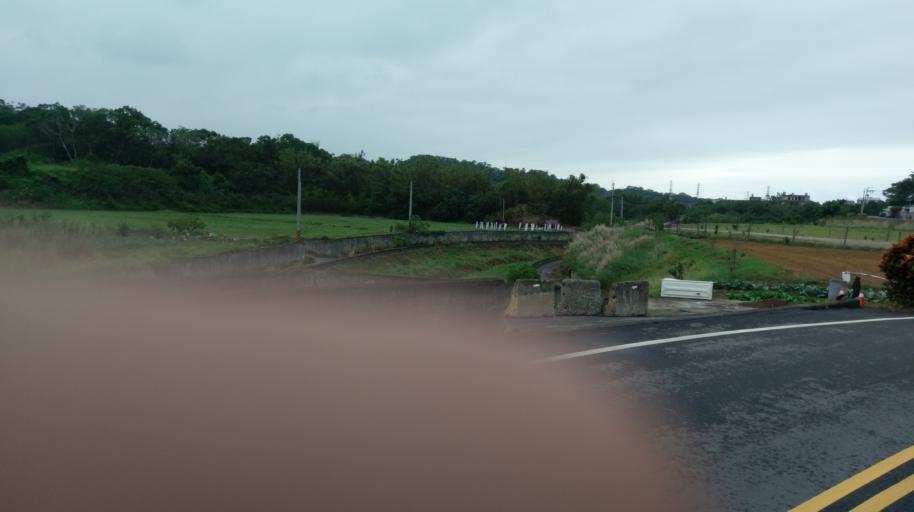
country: TW
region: Taiwan
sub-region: Hsinchu
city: Hsinchu
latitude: 24.7299
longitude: 120.9580
